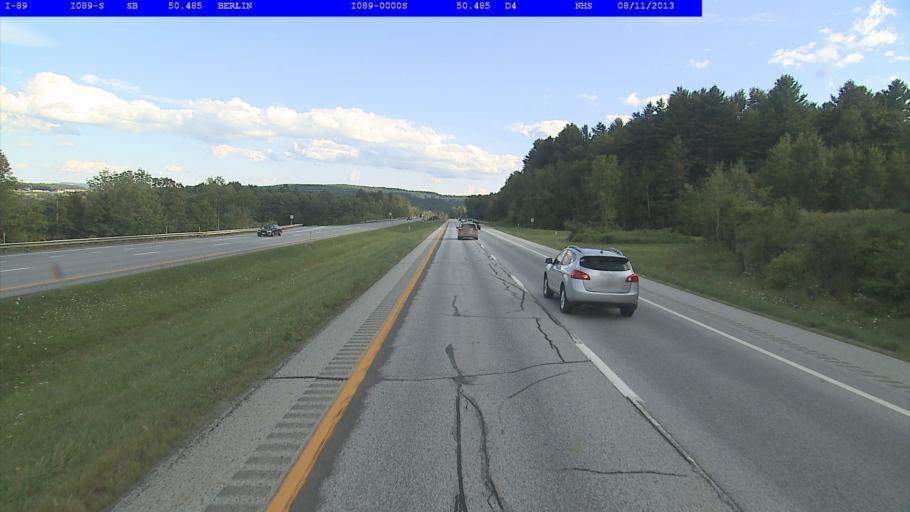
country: US
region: Vermont
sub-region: Washington County
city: Montpelier
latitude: 44.2184
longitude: -72.5844
